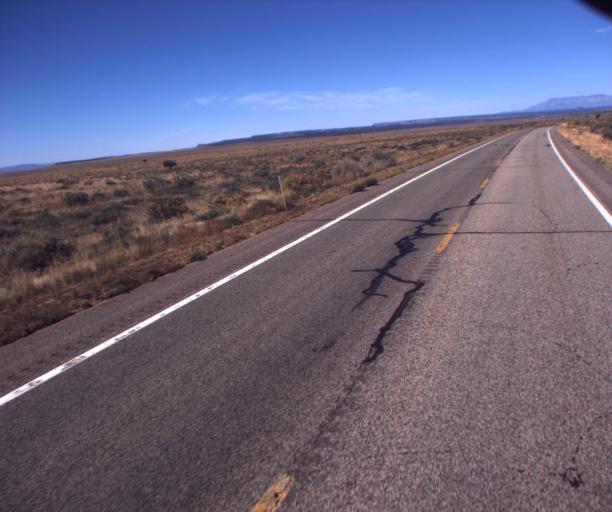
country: US
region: Arizona
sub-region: Mohave County
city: Colorado City
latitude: 36.8865
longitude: -112.9061
